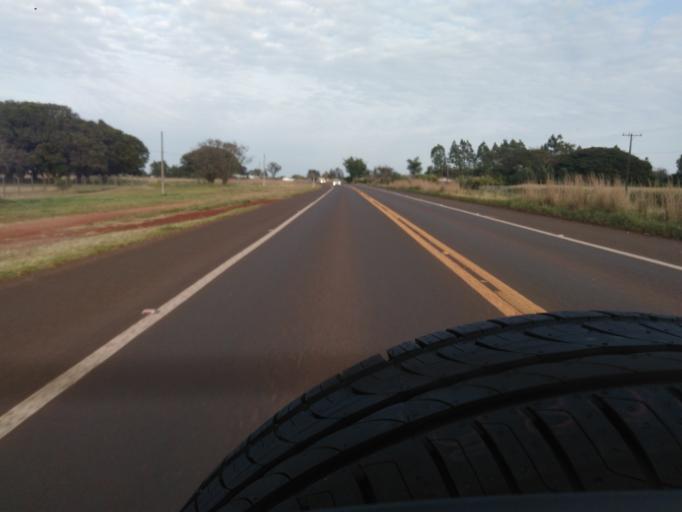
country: BR
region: Mato Grosso do Sul
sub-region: Ponta Pora
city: Ponta Pora
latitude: -22.6191
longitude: -55.6106
